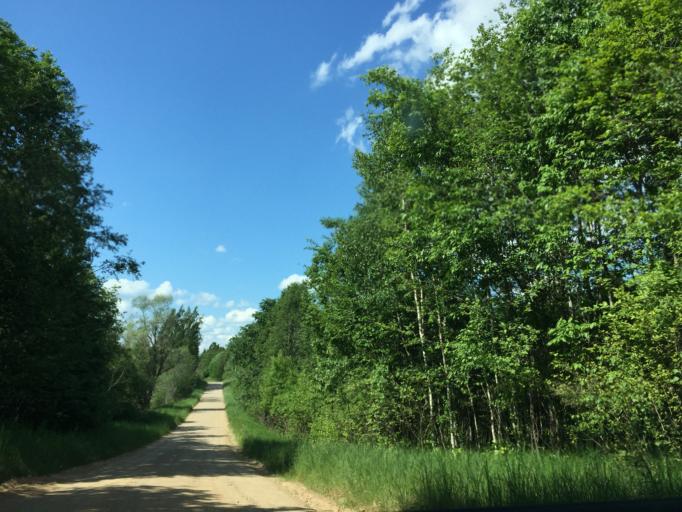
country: LV
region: Priekuli
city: Priekuli
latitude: 57.2547
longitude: 25.3910
